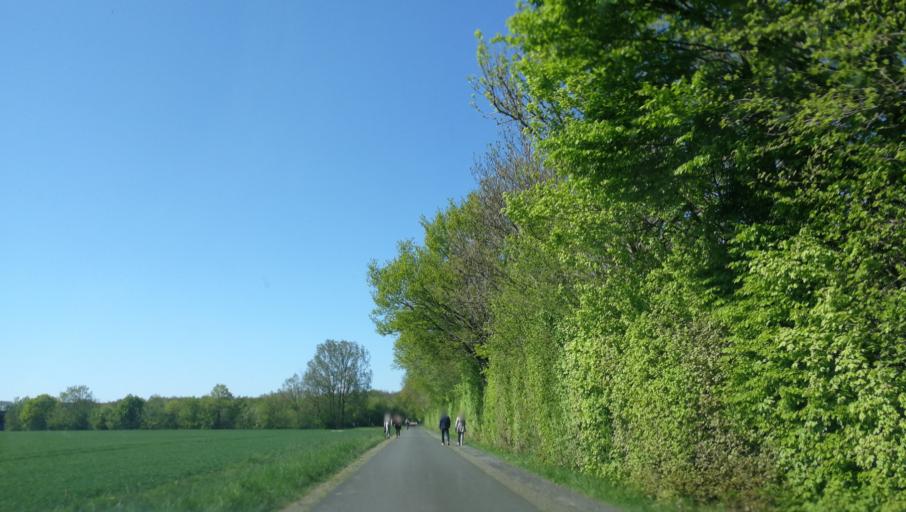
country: DE
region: North Rhine-Westphalia
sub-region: Regierungsbezirk Munster
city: Muenster
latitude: 51.9345
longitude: 7.5571
